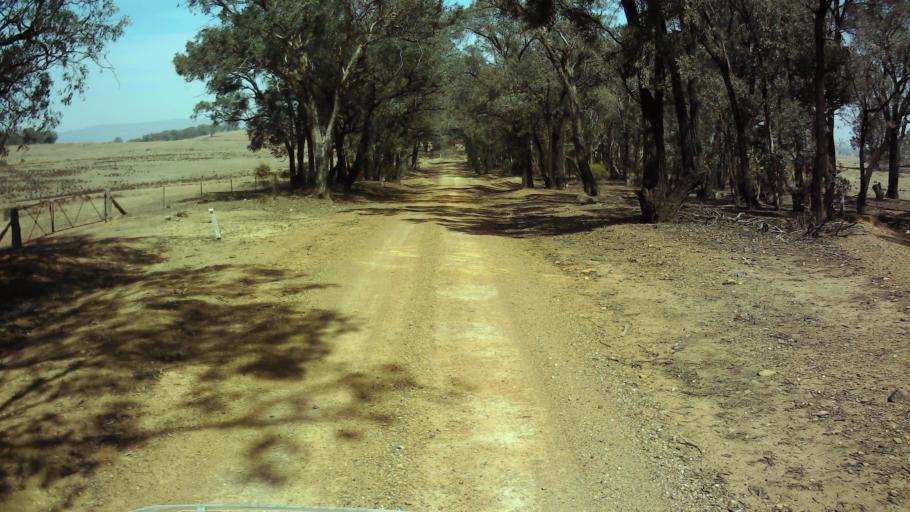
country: AU
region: New South Wales
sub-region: Weddin
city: Grenfell
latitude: -33.8976
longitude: 148.1279
